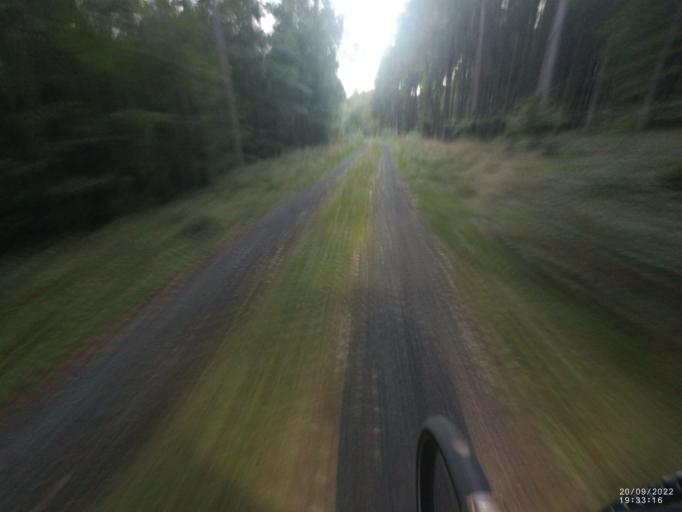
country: DE
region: Rheinland-Pfalz
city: Ellscheid
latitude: 50.1576
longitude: 6.9159
